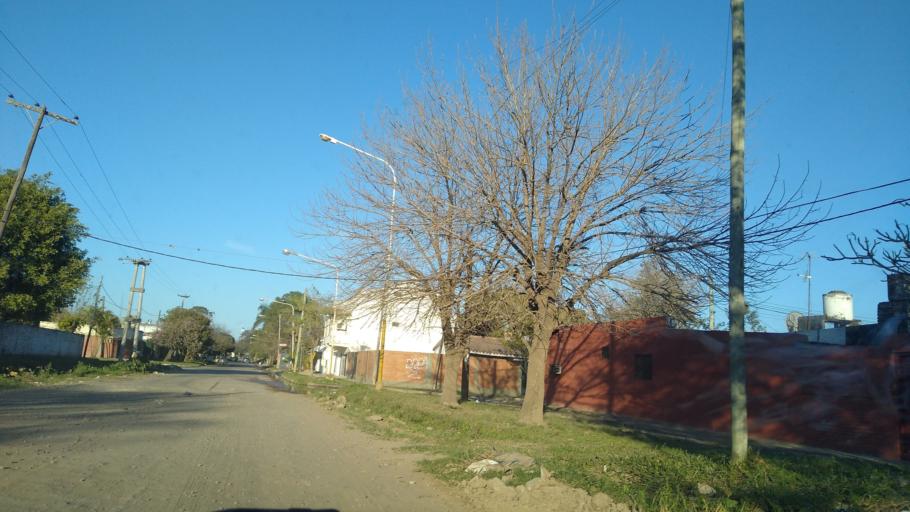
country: AR
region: Chaco
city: Barranqueras
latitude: -27.4801
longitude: -58.9475
